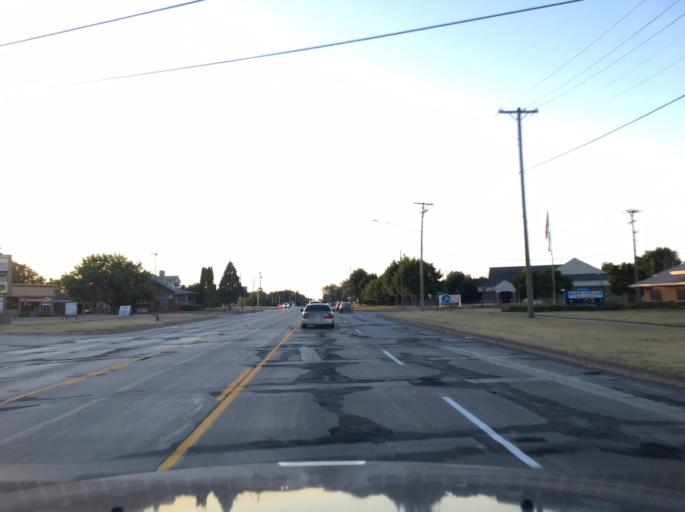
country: US
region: Michigan
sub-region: Macomb County
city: Fraser
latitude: 42.5496
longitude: -82.9589
